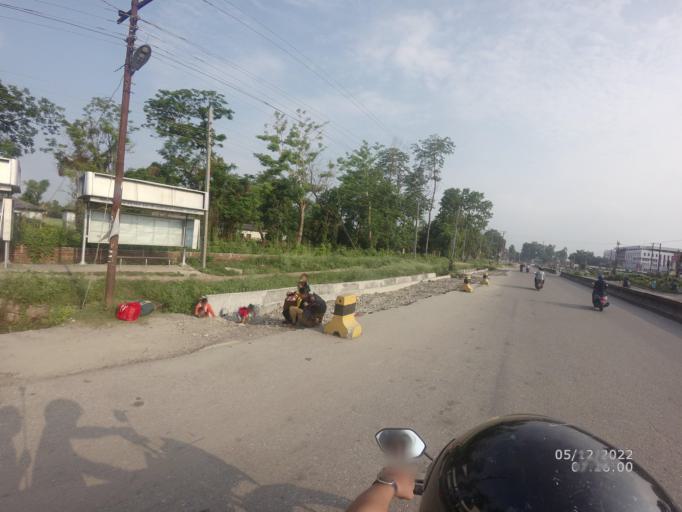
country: NP
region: Central Region
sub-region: Narayani Zone
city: Bharatpur
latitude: 27.6827
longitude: 84.4299
